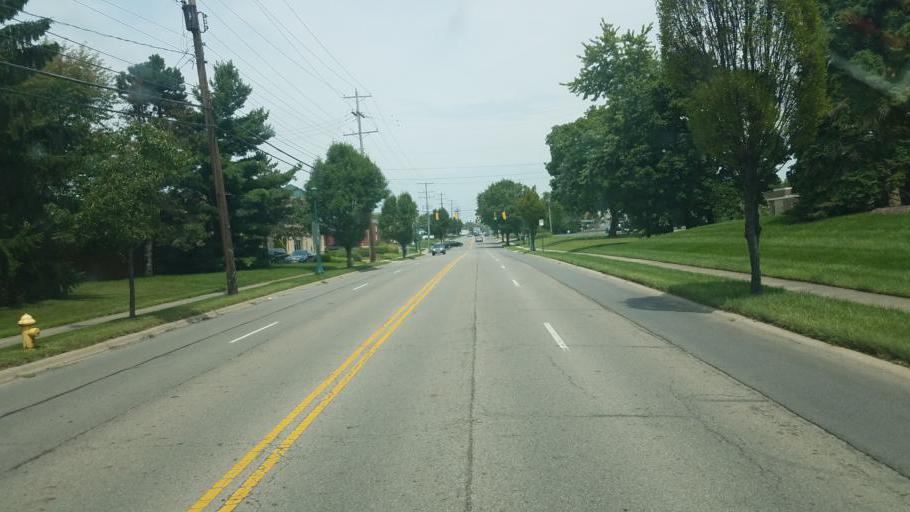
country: US
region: Ohio
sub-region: Franklin County
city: Upper Arlington
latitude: 40.0501
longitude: -83.0668
